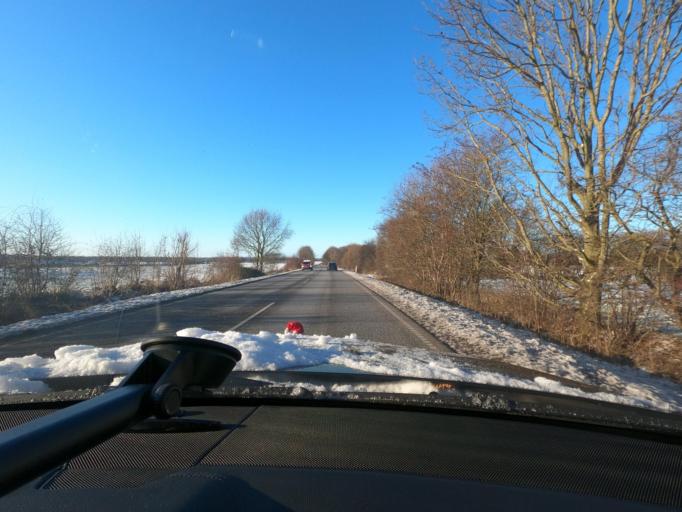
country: DK
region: South Denmark
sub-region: Sonderborg Kommune
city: Horuphav
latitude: 54.9215
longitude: 9.8919
